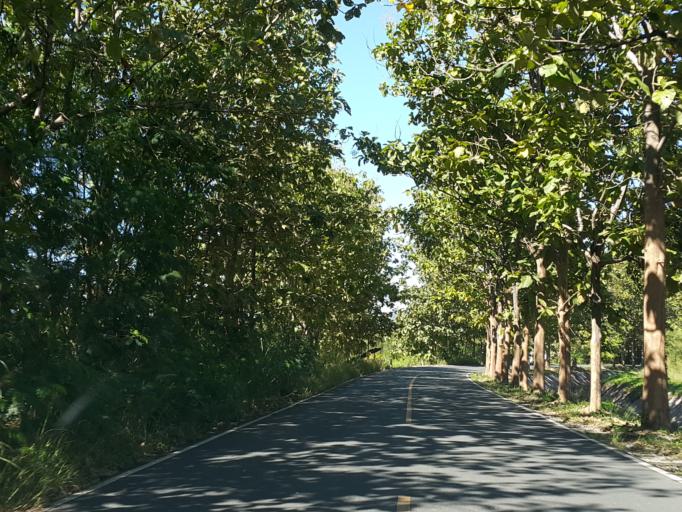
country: TH
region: Chiang Mai
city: San Sai
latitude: 18.8860
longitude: 99.1409
